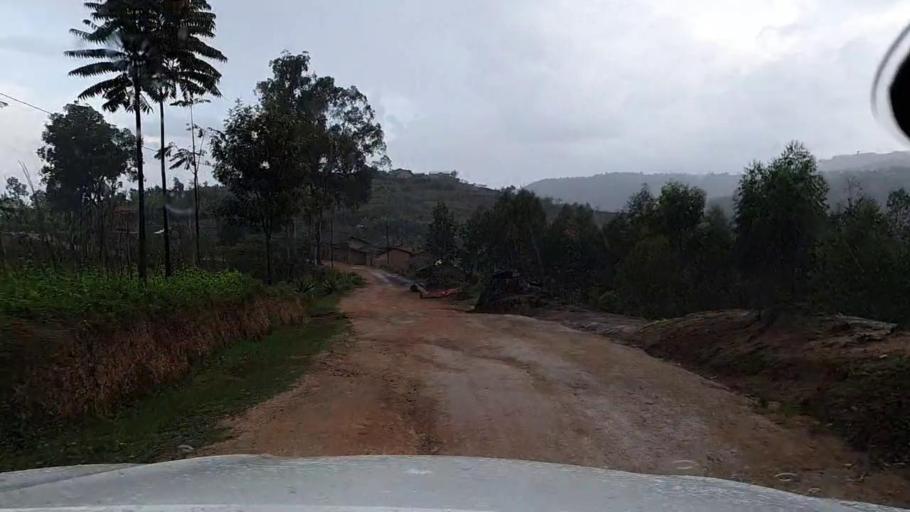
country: BI
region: Kayanza
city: Kayanza
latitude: -2.7762
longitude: 29.5375
